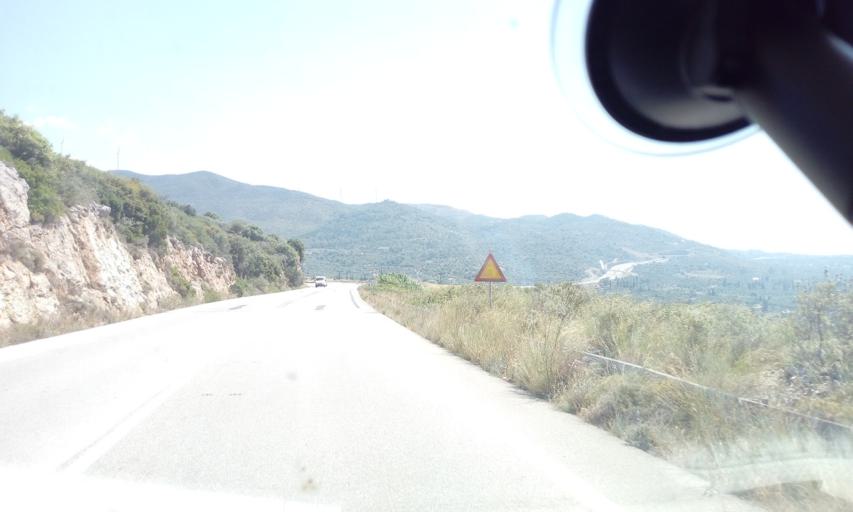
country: GR
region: West Greece
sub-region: Nomos Aitolias kai Akarnanias
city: Antirrio
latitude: 38.3516
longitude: 21.6945
